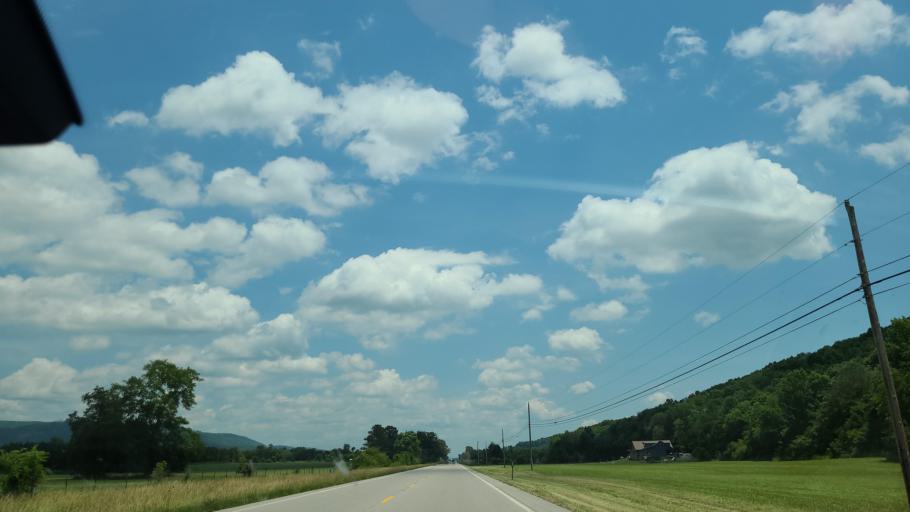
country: US
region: Tennessee
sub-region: Sequatchie County
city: Dunlap
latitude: 35.4773
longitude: -85.3137
